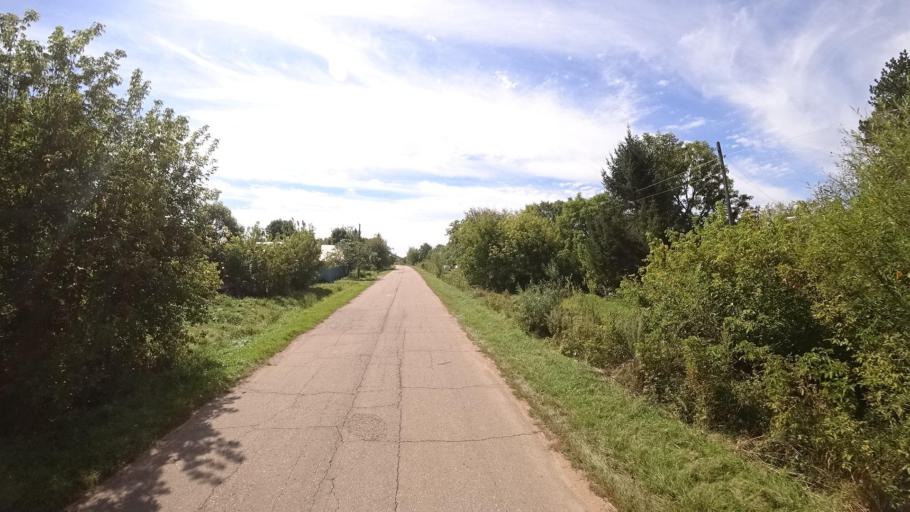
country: RU
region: Primorskiy
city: Kirovskiy
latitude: 44.7572
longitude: 133.6071
